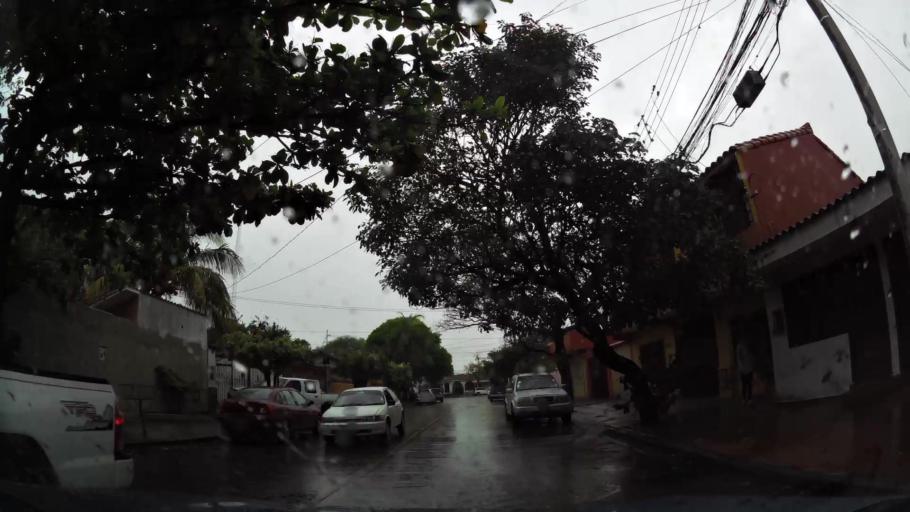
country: BO
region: Santa Cruz
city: Santa Cruz de la Sierra
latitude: -17.7820
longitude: -63.1957
